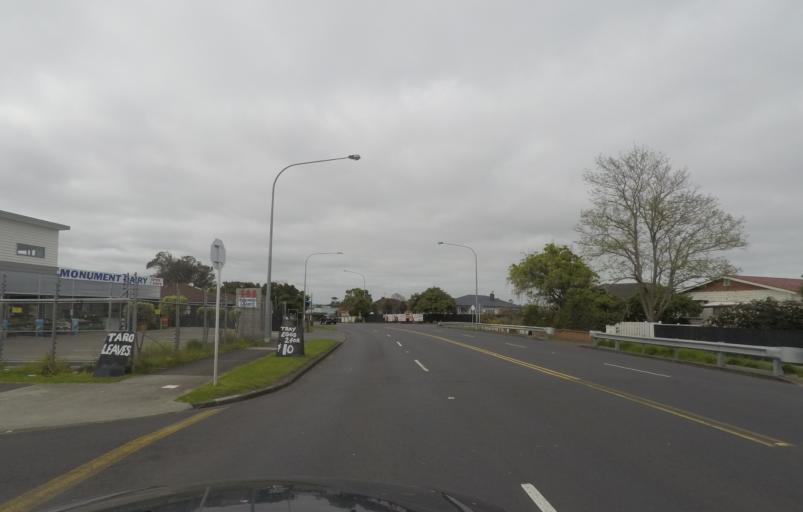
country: NZ
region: Auckland
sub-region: Auckland
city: Wiri
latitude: -36.9521
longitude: 174.8456
